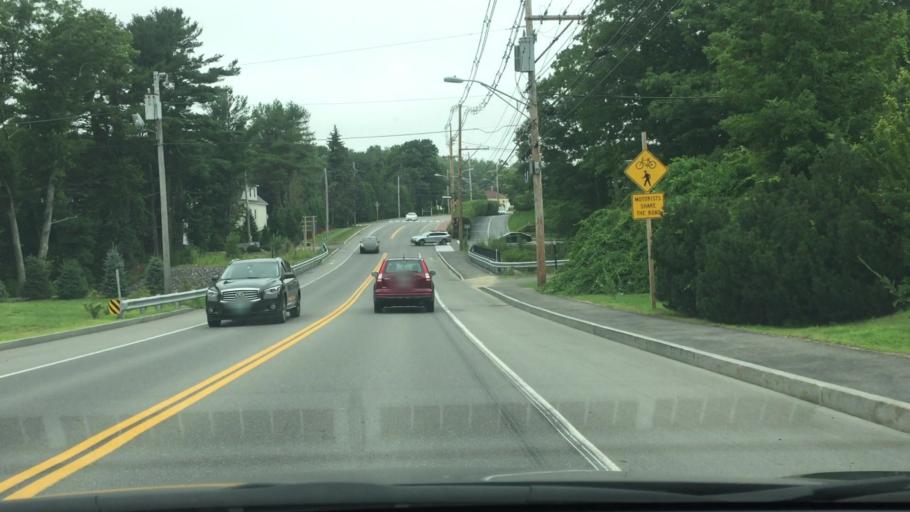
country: US
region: Maine
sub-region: York County
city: Ogunquit
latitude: 43.2404
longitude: -70.6018
